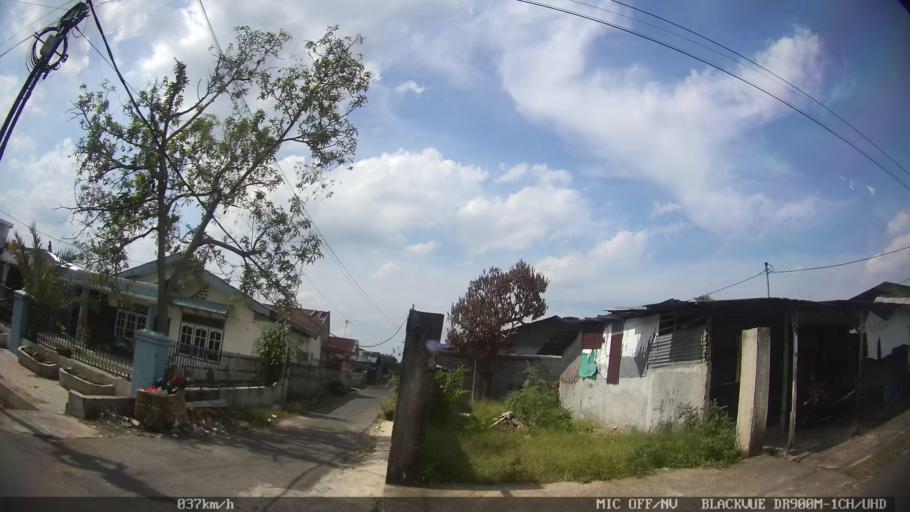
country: ID
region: North Sumatra
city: Binjai
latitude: 3.6131
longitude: 98.5104
